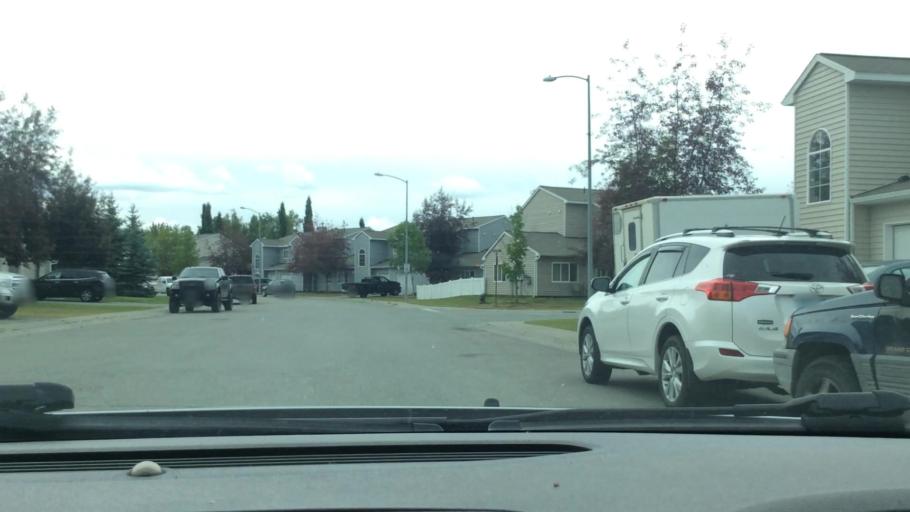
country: US
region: Alaska
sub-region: Anchorage Municipality
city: Anchorage
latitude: 61.2342
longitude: -149.7721
